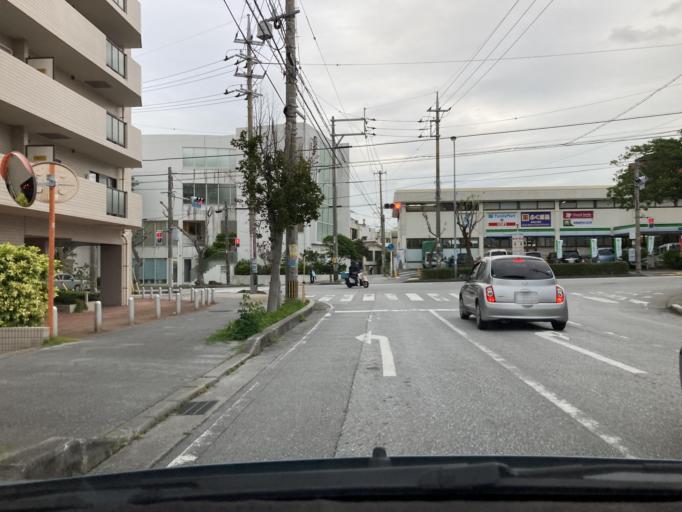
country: JP
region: Okinawa
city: Naha-shi
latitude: 26.2089
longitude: 127.6821
